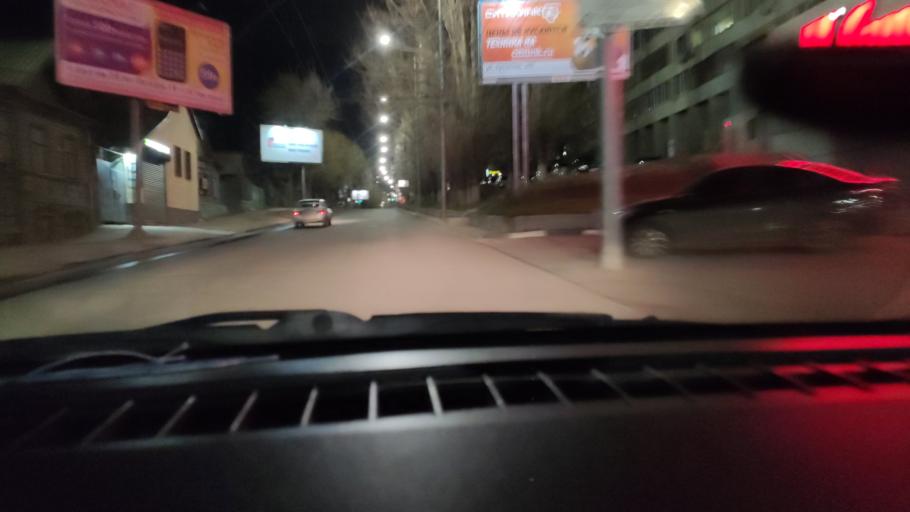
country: RU
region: Saratov
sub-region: Saratovskiy Rayon
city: Saratov
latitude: 51.5315
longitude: 46.0613
